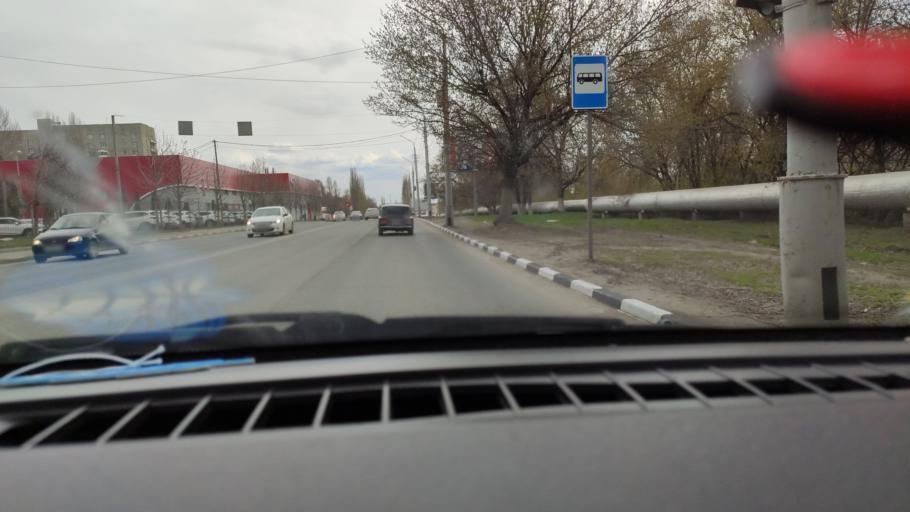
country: RU
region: Saratov
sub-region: Saratovskiy Rayon
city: Saratov
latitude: 51.5693
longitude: 45.9962
